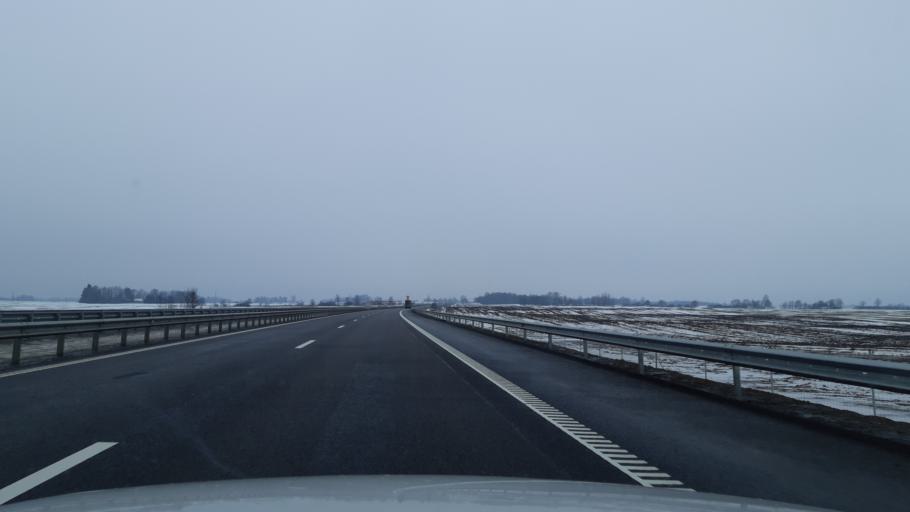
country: LT
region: Kauno apskritis
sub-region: Kauno rajonas
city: Mastaiciai
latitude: 54.7443
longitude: 23.7197
